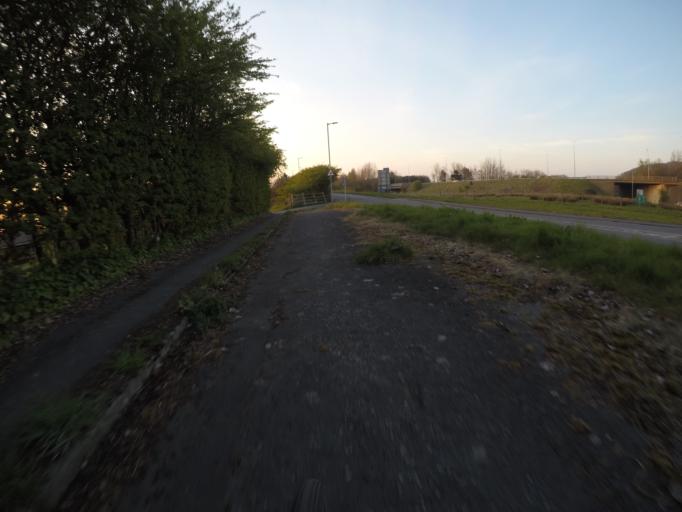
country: GB
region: Scotland
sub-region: South Ayrshire
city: Troon
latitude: 55.5678
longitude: -4.6391
